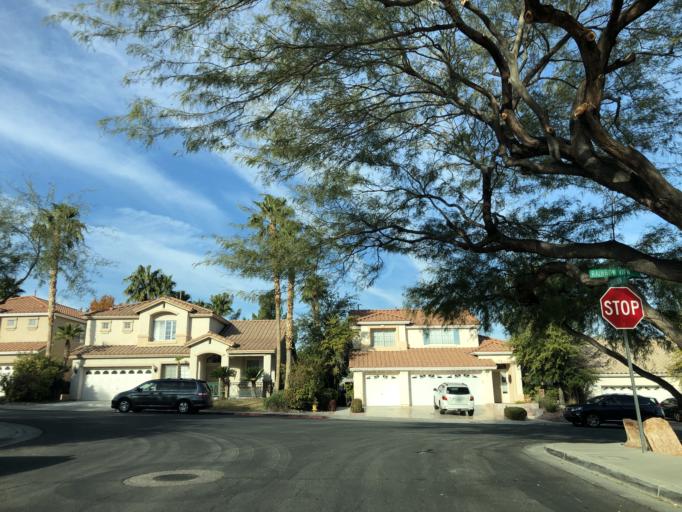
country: US
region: Nevada
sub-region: Clark County
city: Whitney
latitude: 36.0225
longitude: -115.0743
